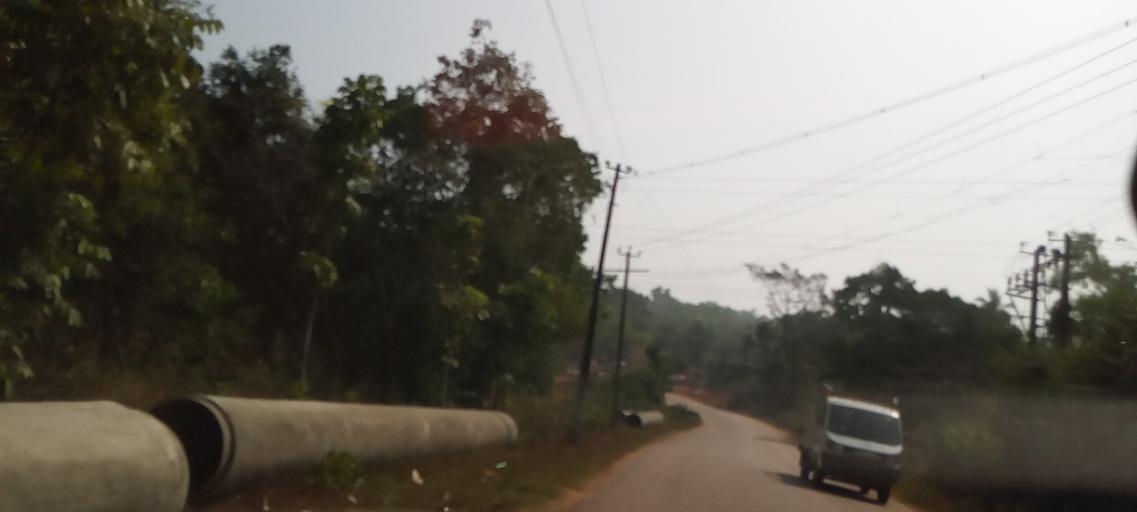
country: IN
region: Karnataka
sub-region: Udupi
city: Manipala
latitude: 13.5126
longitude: 74.8395
